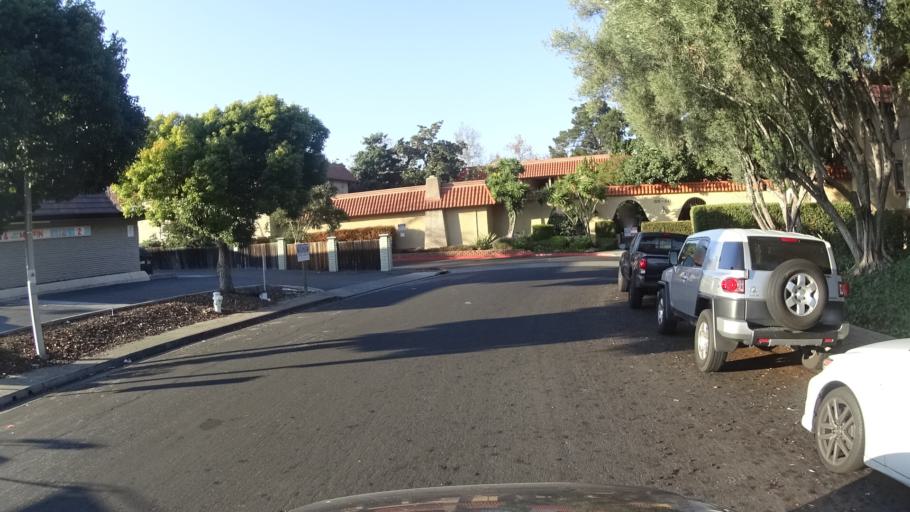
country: US
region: California
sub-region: Santa Clara County
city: Santa Clara
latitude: 37.3458
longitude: -121.9940
